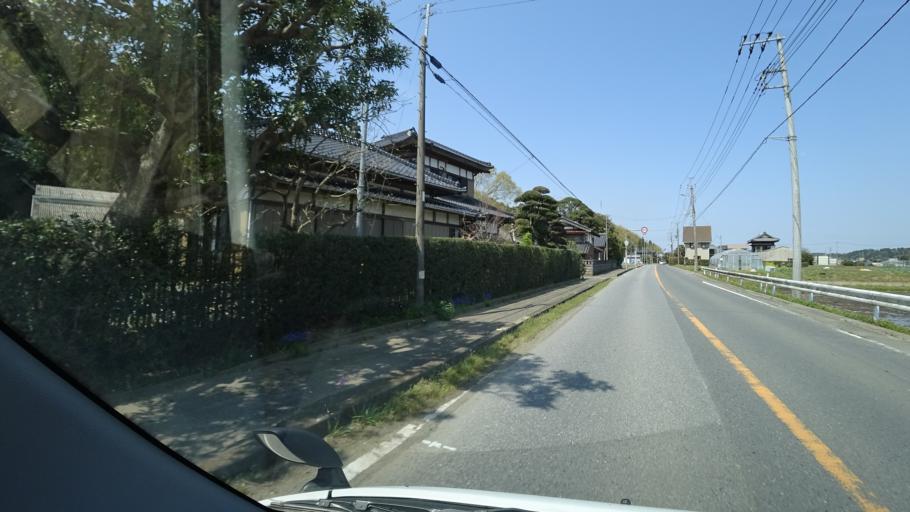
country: JP
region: Chiba
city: Yokaichiba
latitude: 35.6723
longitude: 140.4699
